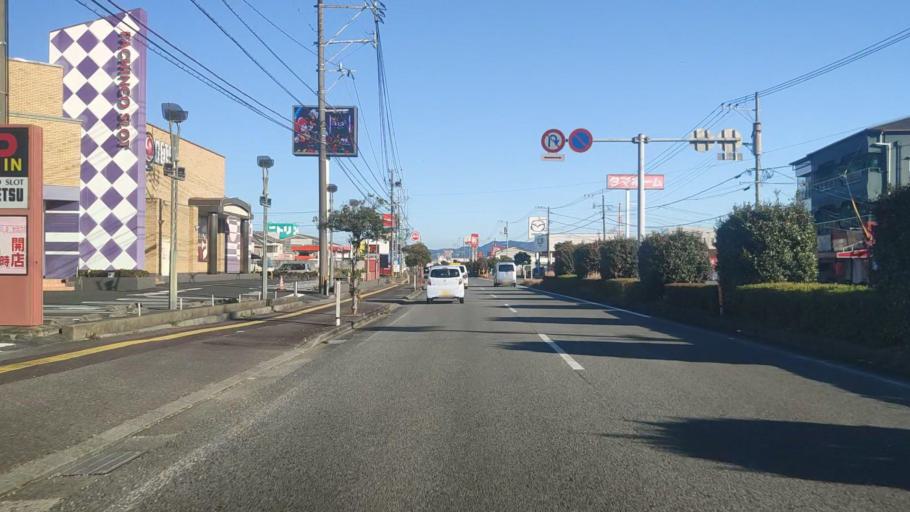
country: JP
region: Miyazaki
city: Nobeoka
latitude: 32.5542
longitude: 131.6791
